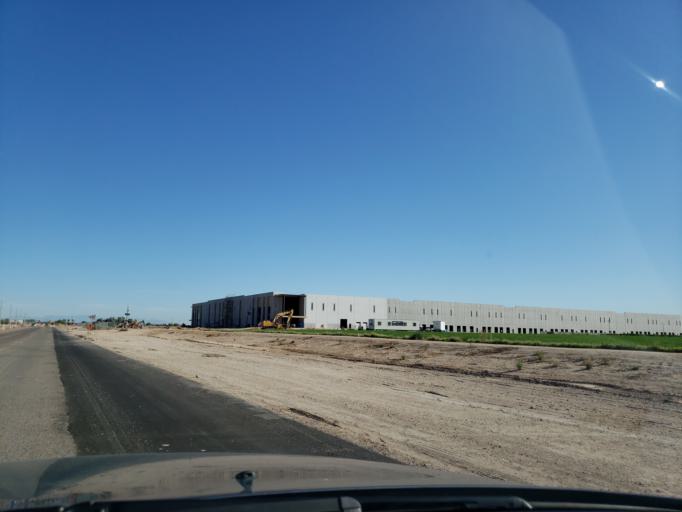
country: US
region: Arizona
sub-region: Maricopa County
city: Goodyear
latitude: 33.4413
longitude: -112.3755
